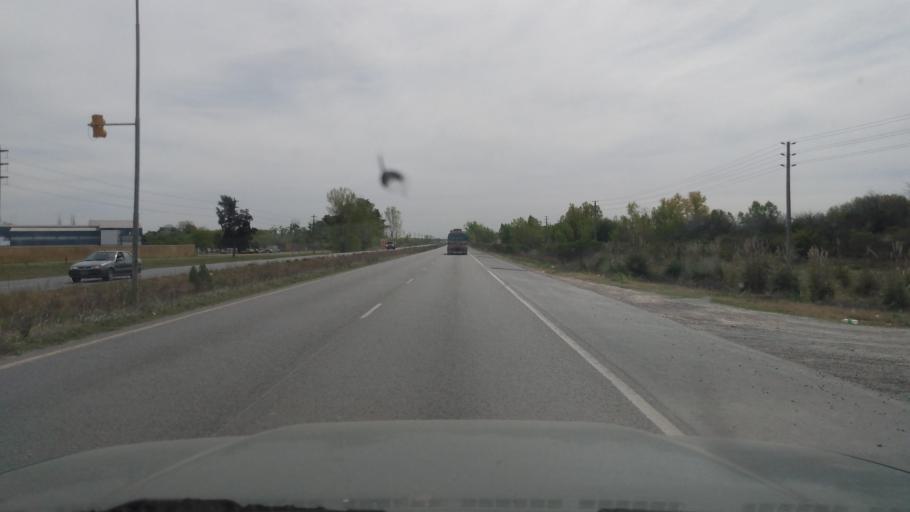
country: AR
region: Buenos Aires
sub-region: Partido de Lujan
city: Lujan
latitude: -34.5515
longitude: -59.0366
